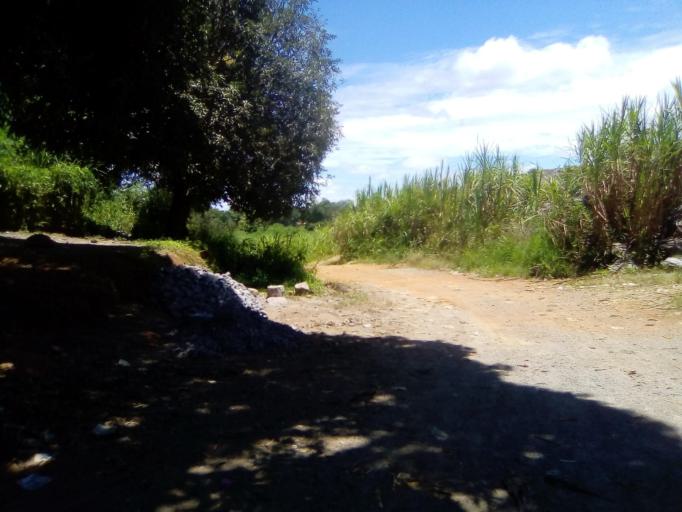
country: SL
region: Eastern Province
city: Koidu
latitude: 8.6351
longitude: -10.9735
